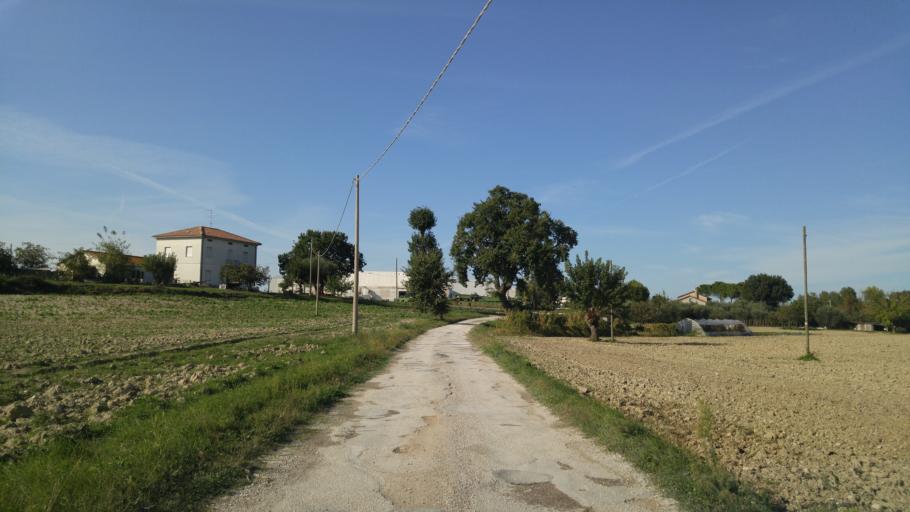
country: IT
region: The Marches
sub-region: Provincia di Pesaro e Urbino
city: Bellocchi
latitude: 43.7923
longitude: 13.0227
